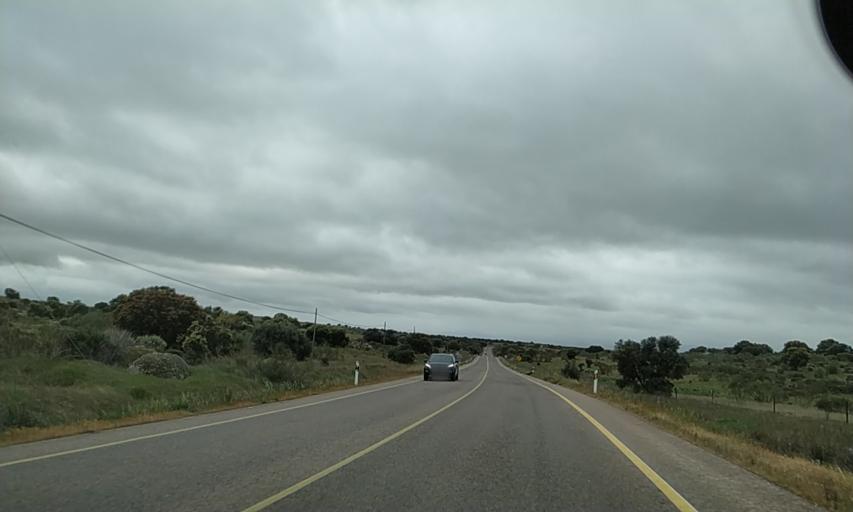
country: ES
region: Extremadura
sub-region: Provincia de Caceres
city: Caceres
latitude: 39.4209
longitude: -6.4130
